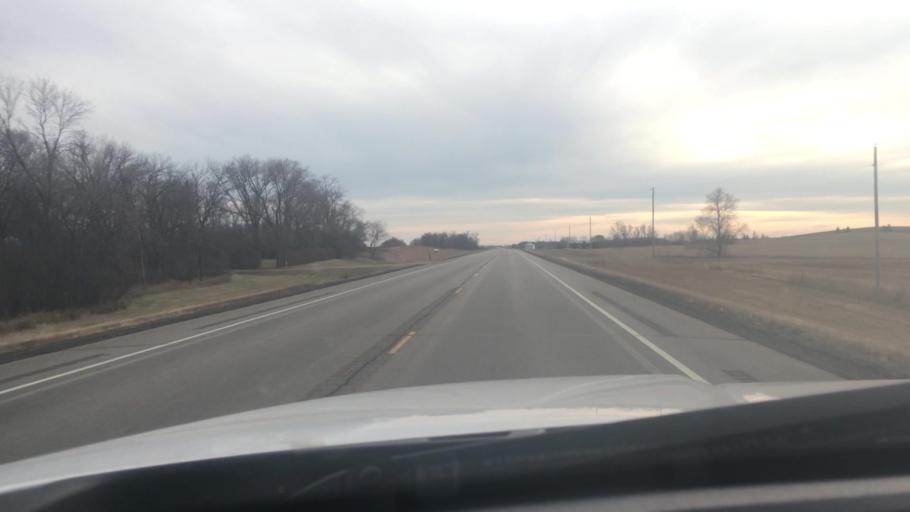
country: US
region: Minnesota
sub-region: Otter Tail County
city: Perham
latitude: 46.3306
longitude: -95.7185
